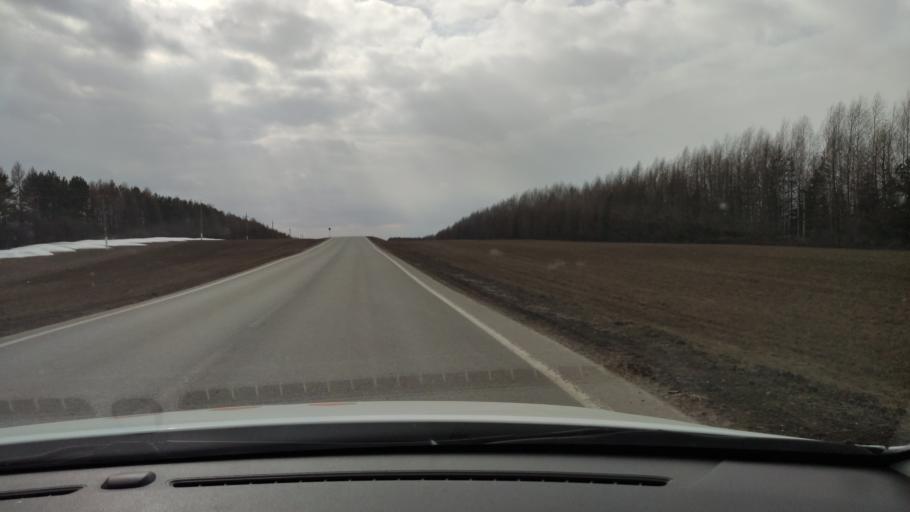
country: RU
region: Tatarstan
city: Vysokaya Gora
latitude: 56.2265
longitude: 49.2938
